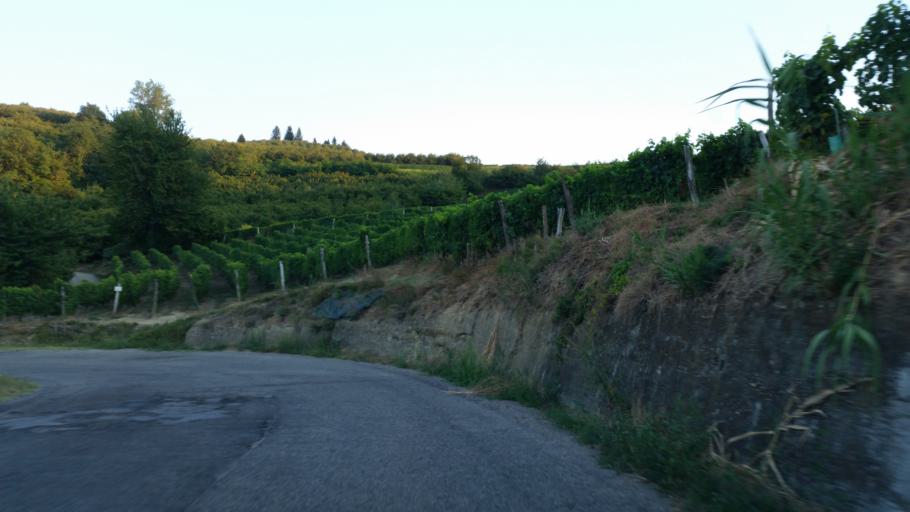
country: IT
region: Piedmont
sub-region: Provincia di Cuneo
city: Mango
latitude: 44.6767
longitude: 8.1389
